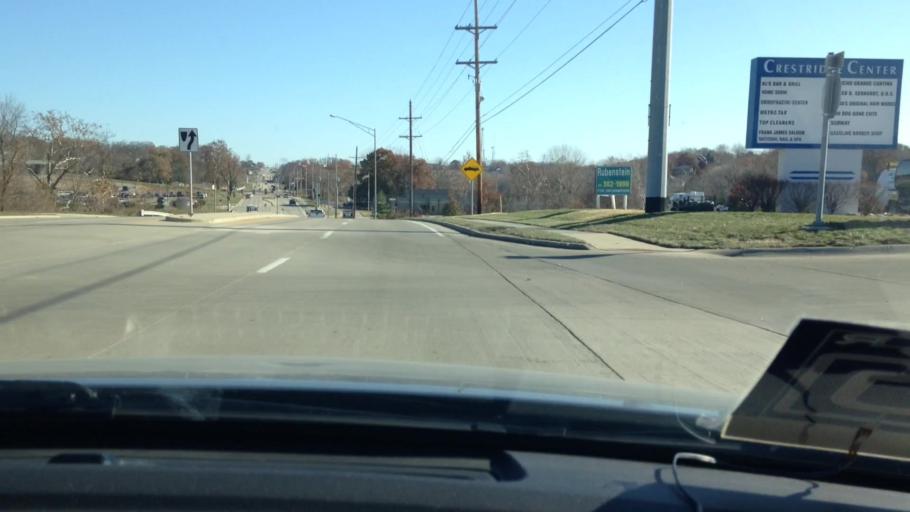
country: US
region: Missouri
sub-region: Platte County
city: Parkville
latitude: 39.2097
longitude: -94.7084
